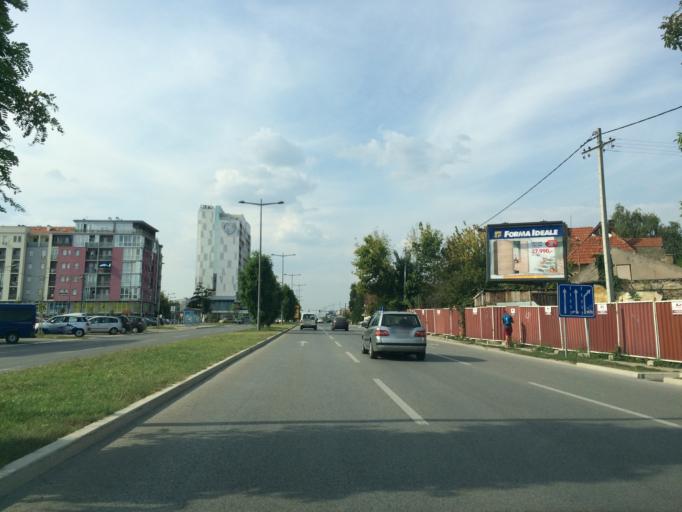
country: RS
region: Autonomna Pokrajina Vojvodina
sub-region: Juznobacki Okrug
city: Novi Sad
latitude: 45.2462
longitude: 19.8183
